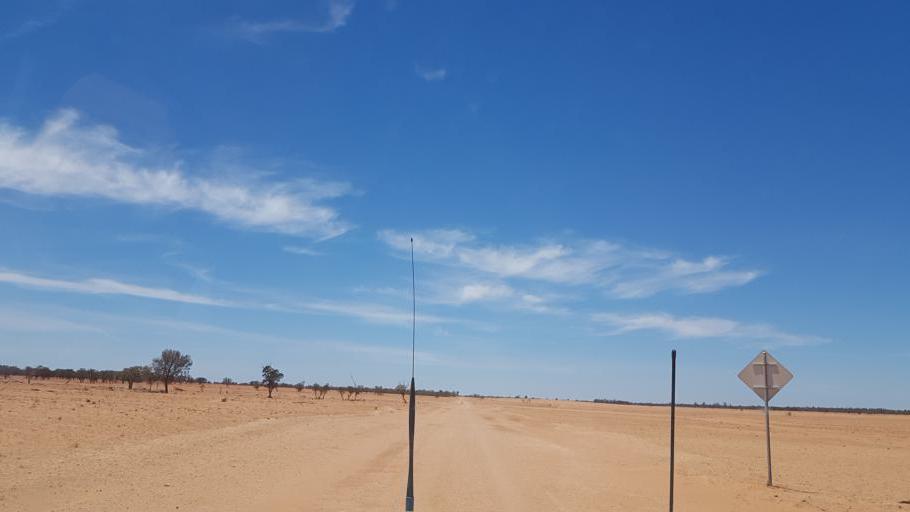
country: AU
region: New South Wales
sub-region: Wentworth
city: Dareton
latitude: -33.3496
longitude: 141.4641
